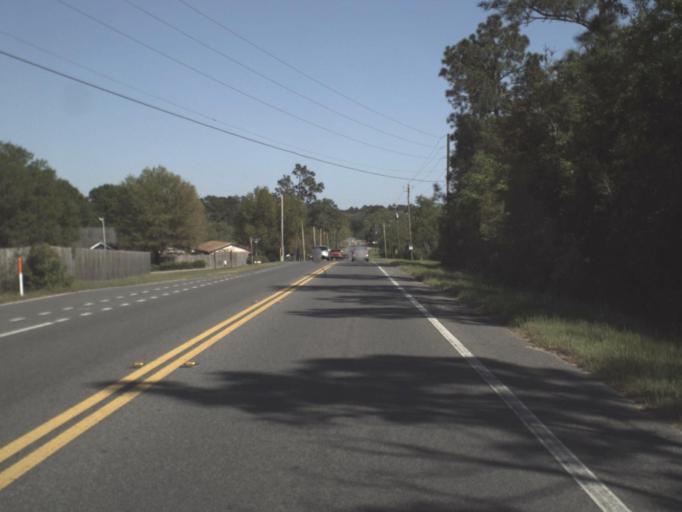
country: US
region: Florida
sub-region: Escambia County
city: Bellview
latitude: 30.5010
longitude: -87.3443
